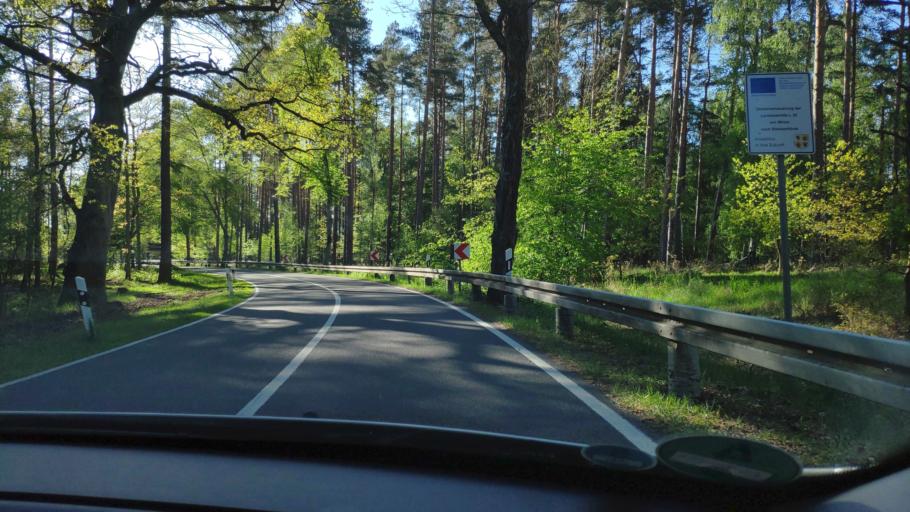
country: DE
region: Mecklenburg-Vorpommern
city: Wesenberg
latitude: 53.3294
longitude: 12.9208
